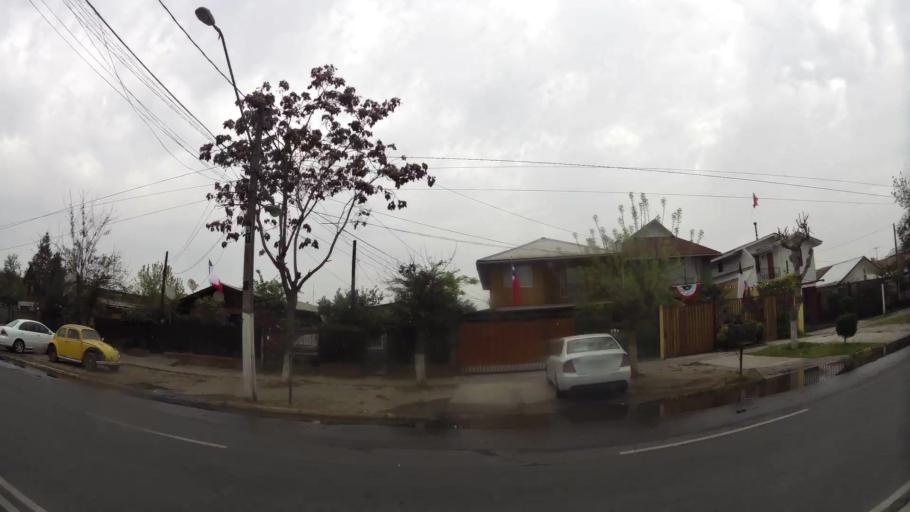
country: CL
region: Santiago Metropolitan
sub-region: Provincia de Santiago
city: Villa Presidente Frei, Nunoa, Santiago, Chile
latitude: -33.4923
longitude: -70.6065
